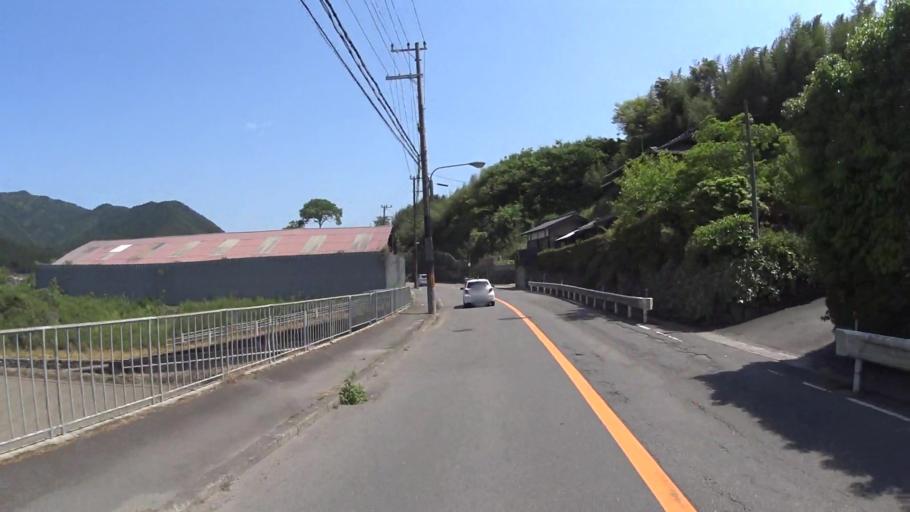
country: JP
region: Kyoto
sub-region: Kyoto-shi
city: Kamigyo-ku
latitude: 35.1095
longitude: 135.8245
